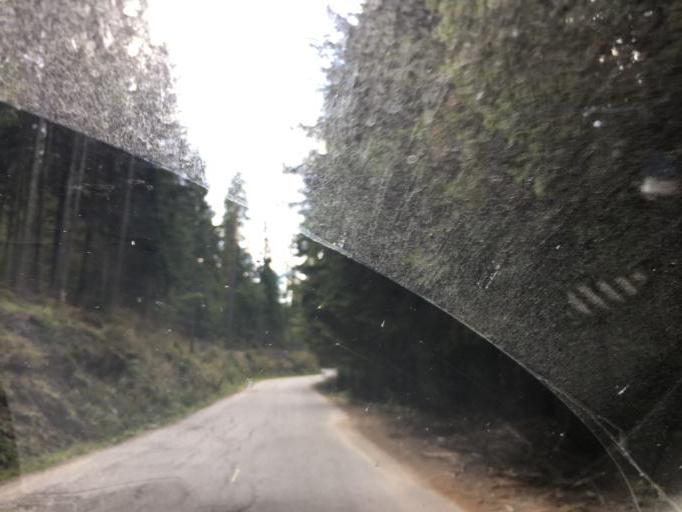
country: BG
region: Pazardzhik
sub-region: Obshtina Batak
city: Batak
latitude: 41.9117
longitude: 24.2873
